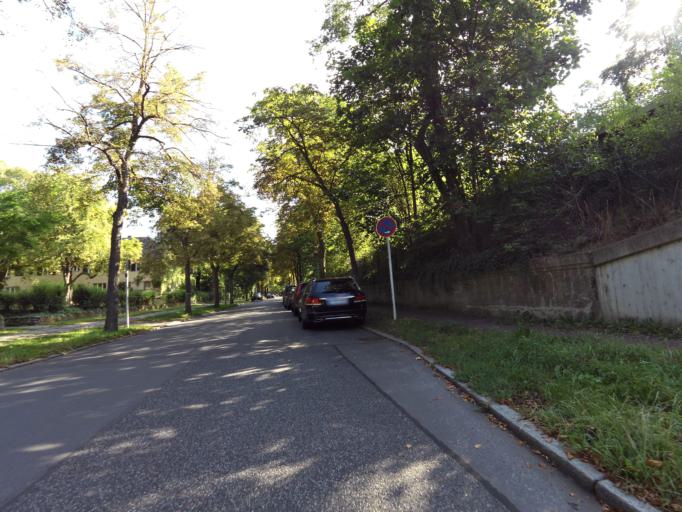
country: DE
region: Berlin
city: Nikolassee
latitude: 52.4376
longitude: 13.2055
